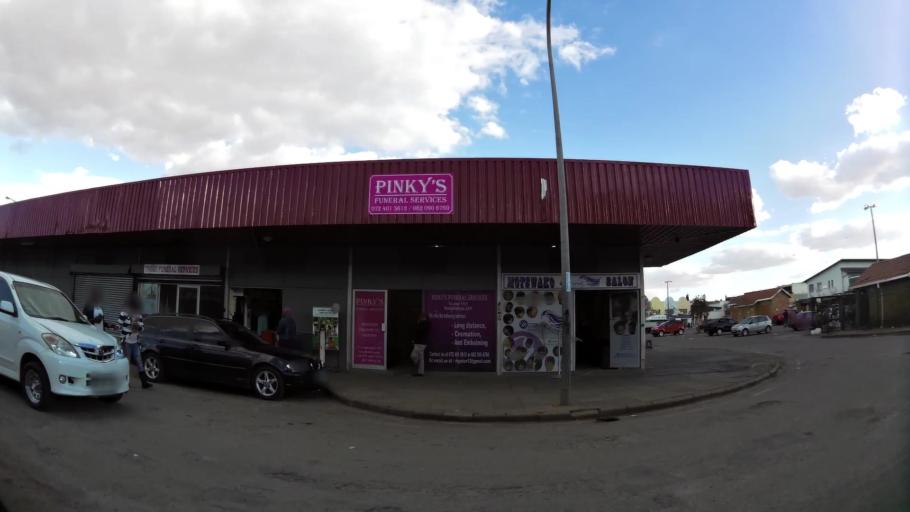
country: ZA
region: North-West
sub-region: Dr Kenneth Kaunda District Municipality
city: Potchefstroom
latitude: -26.7124
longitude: 27.0987
